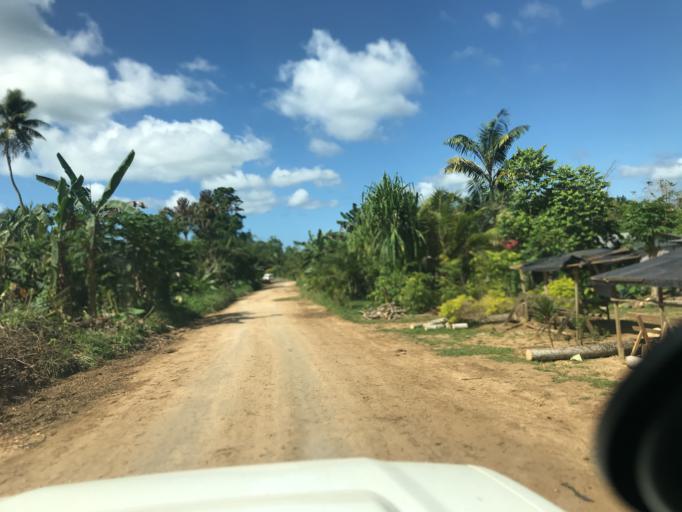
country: VU
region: Sanma
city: Luganville
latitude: -15.5308
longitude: 167.1515
